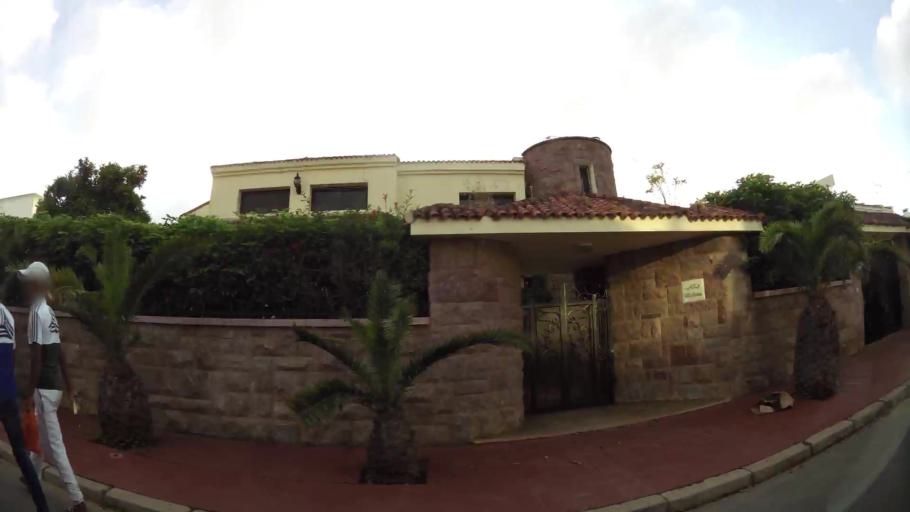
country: MA
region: Rabat-Sale-Zemmour-Zaer
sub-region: Rabat
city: Rabat
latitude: 33.9614
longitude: -6.8501
